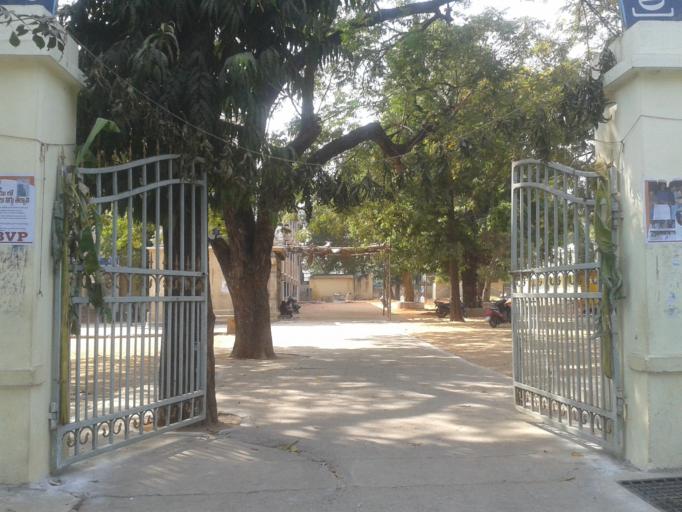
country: IN
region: Andhra Pradesh
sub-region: Chittoor
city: Tirupati
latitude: 13.6405
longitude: 79.4187
